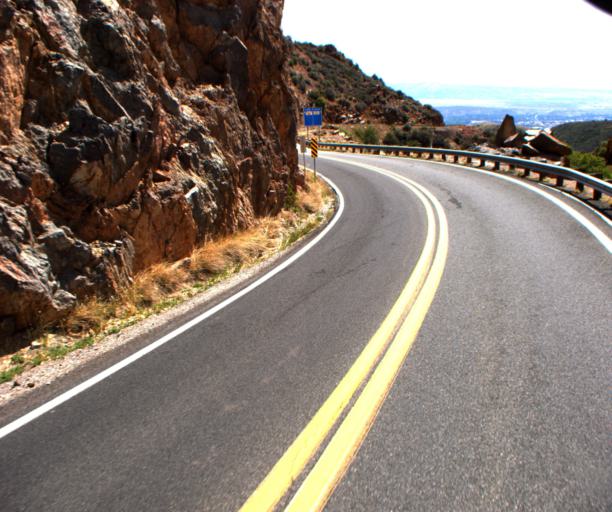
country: US
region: Arizona
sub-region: Yavapai County
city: Clarkdale
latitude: 34.7439
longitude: -112.1200
